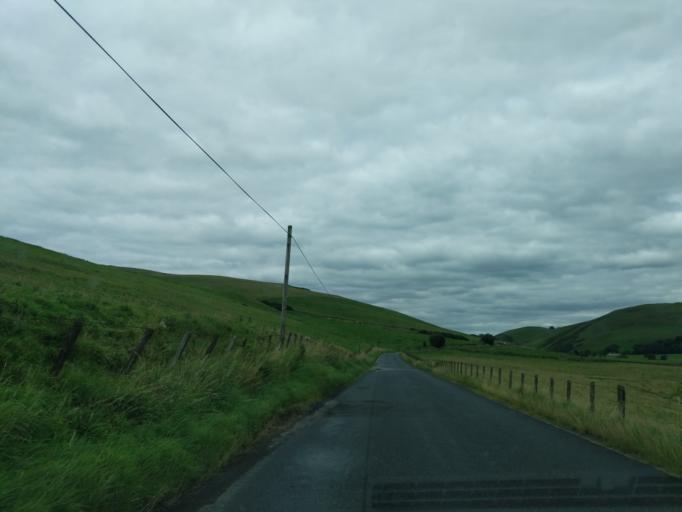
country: GB
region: Scotland
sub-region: The Scottish Borders
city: West Linton
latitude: 55.6823
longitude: -3.3340
